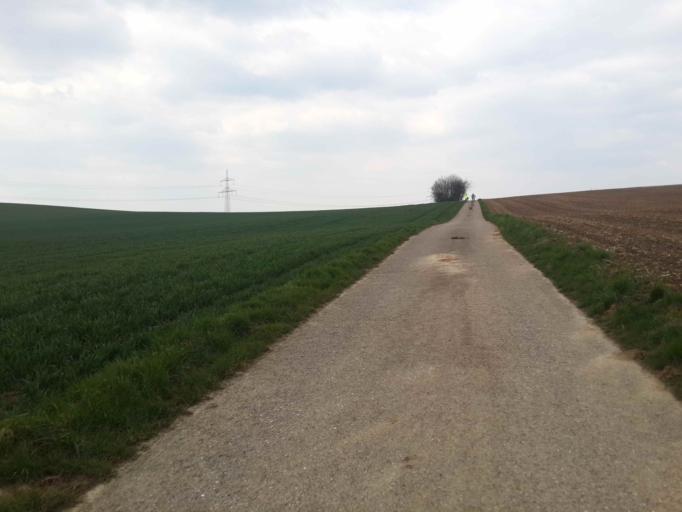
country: DE
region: Baden-Wuerttemberg
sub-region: Regierungsbezirk Stuttgart
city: Eppingen
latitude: 49.1643
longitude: 8.9168
